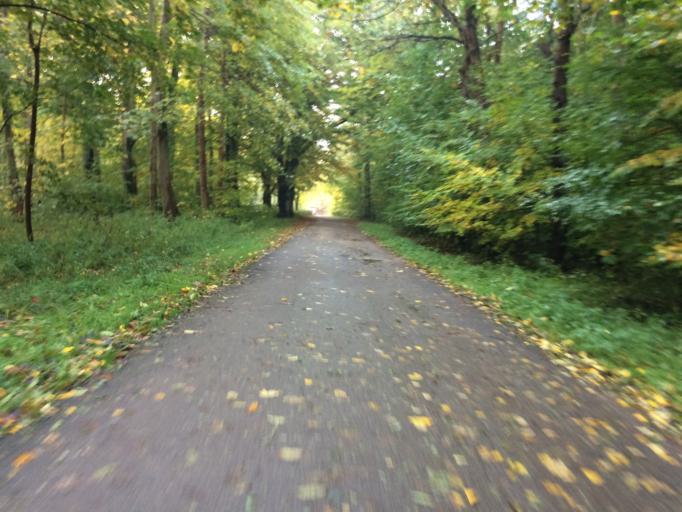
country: DK
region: Zealand
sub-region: Ringsted Kommune
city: Ringsted
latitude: 55.4893
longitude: 11.8034
